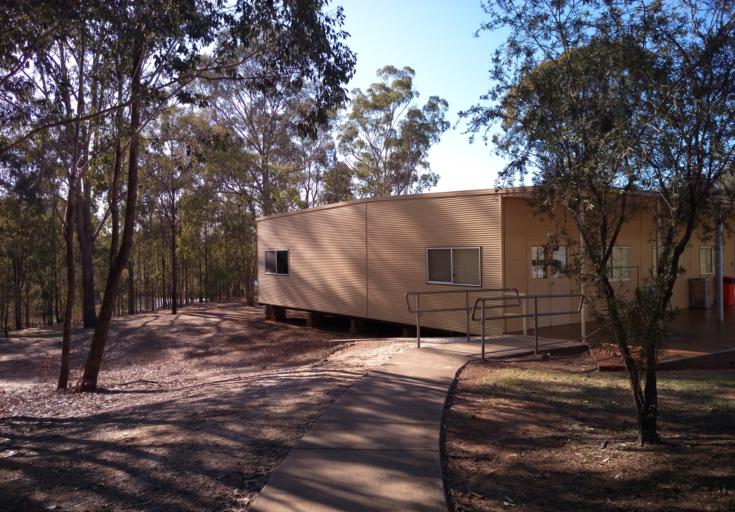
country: AU
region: Queensland
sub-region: Ipswich
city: Brassall
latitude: -27.5868
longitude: 152.7053
